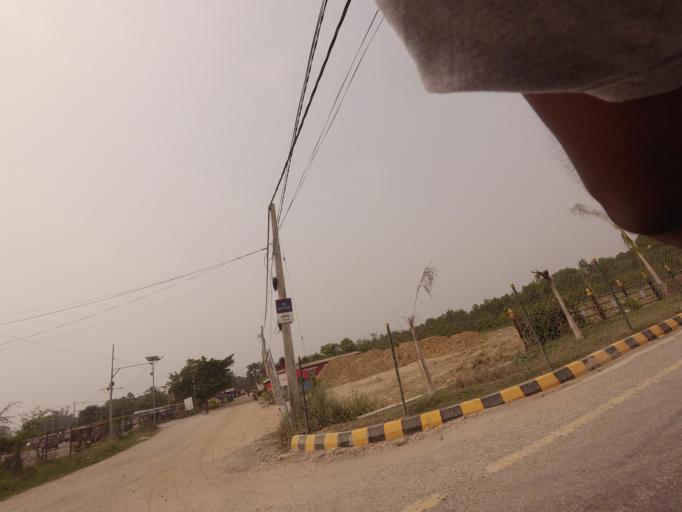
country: IN
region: Uttar Pradesh
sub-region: Maharajganj
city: Nautanwa
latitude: 27.4915
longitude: 83.2744
